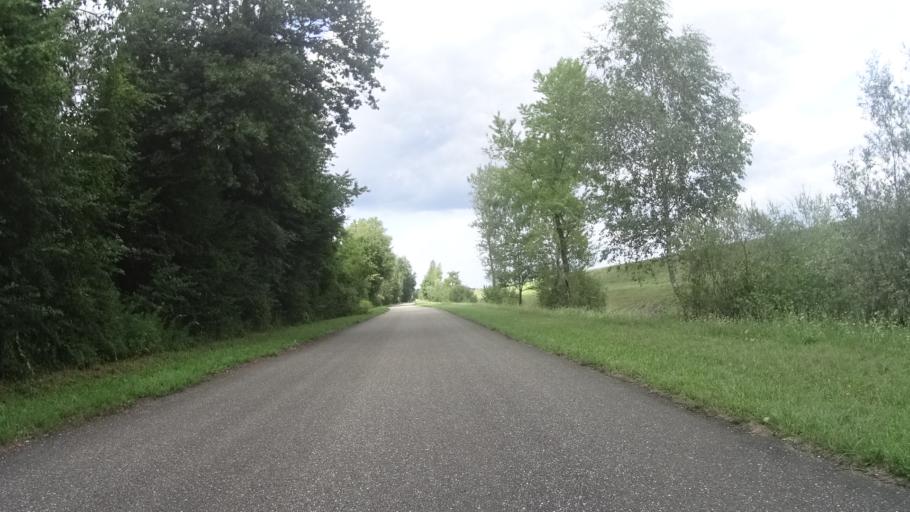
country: DE
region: Baden-Wuerttemberg
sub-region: Karlsruhe Region
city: Rheinmuenster
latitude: 48.7724
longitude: 8.0217
